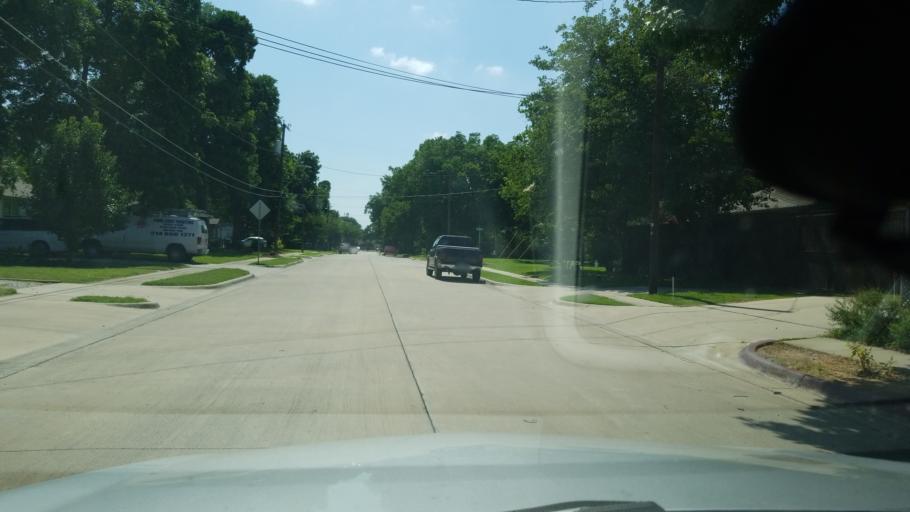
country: US
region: Texas
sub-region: Dallas County
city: Irving
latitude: 32.8165
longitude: -96.9560
